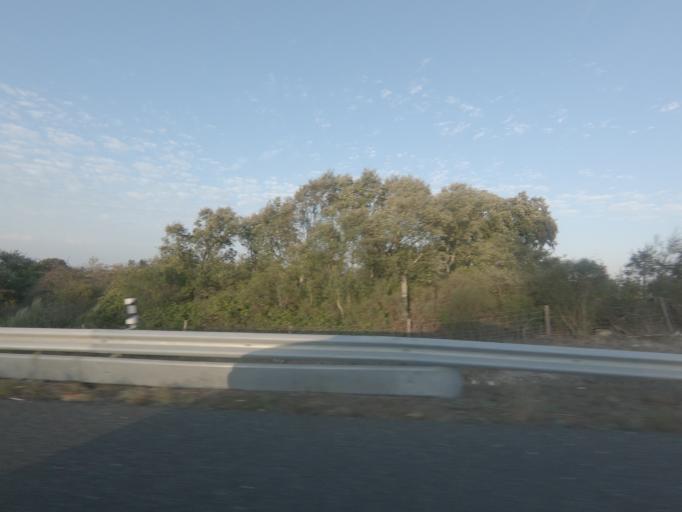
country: PT
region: Leiria
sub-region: Leiria
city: Santa Catarina da Serra
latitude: 39.6795
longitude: -8.6835
